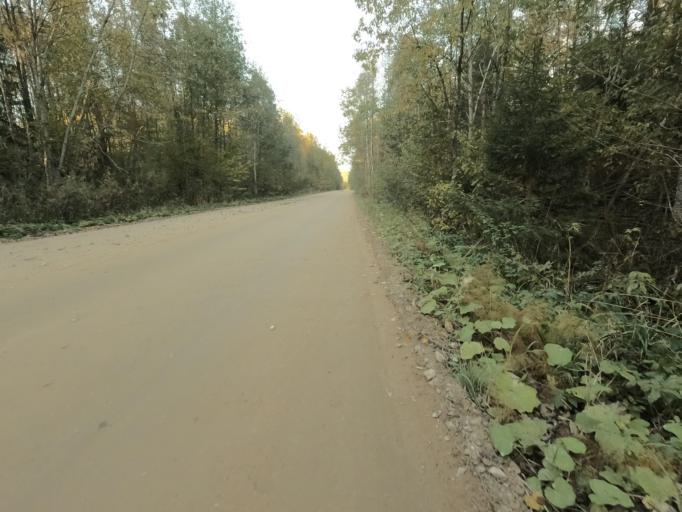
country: RU
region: Leningrad
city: Lyuban'
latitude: 58.9884
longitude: 31.1016
